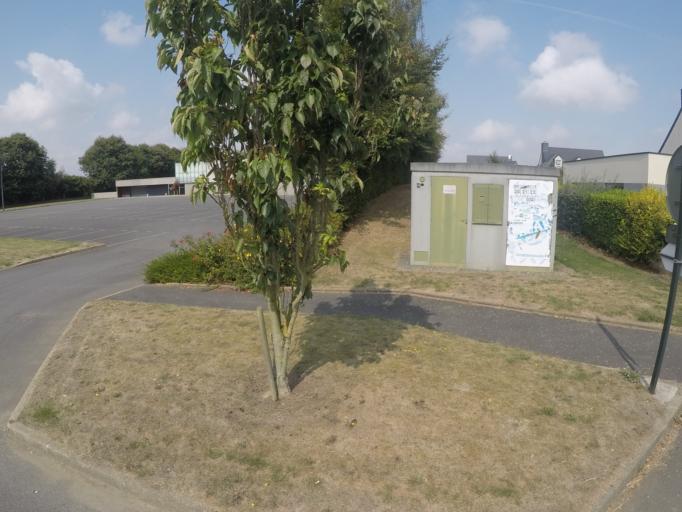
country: FR
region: Brittany
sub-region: Departement des Cotes-d'Armor
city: Tremuson
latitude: 48.5154
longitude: -2.8872
